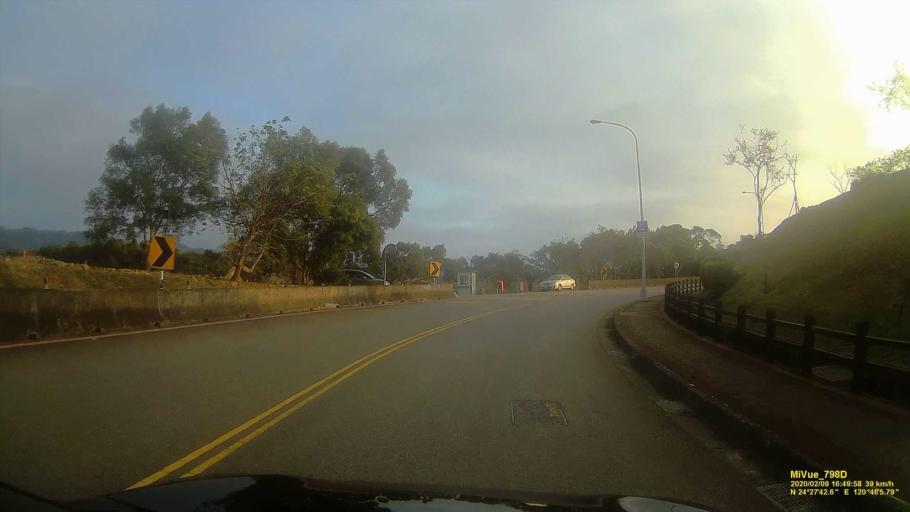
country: TW
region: Taiwan
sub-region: Miaoli
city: Miaoli
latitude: 24.4616
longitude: 120.7683
